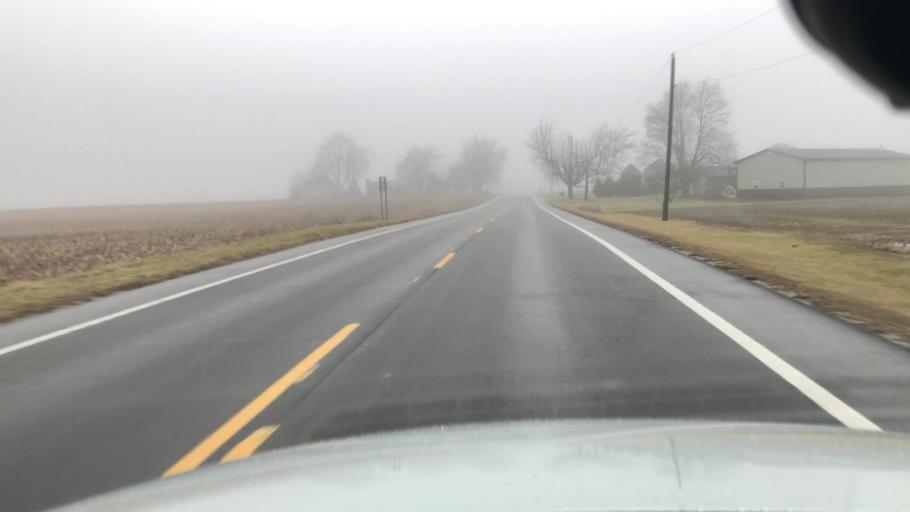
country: US
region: Ohio
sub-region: Logan County
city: Lakeview
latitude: 40.6033
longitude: -83.8816
